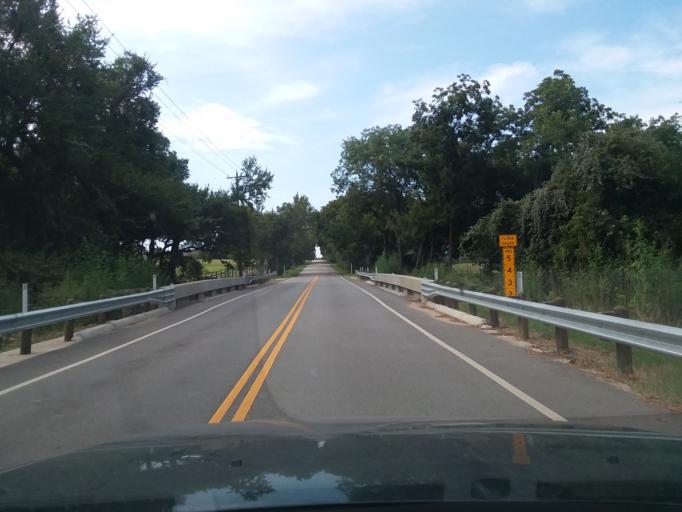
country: US
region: Texas
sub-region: Denton County
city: Bartonville
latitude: 33.1082
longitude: -97.1312
